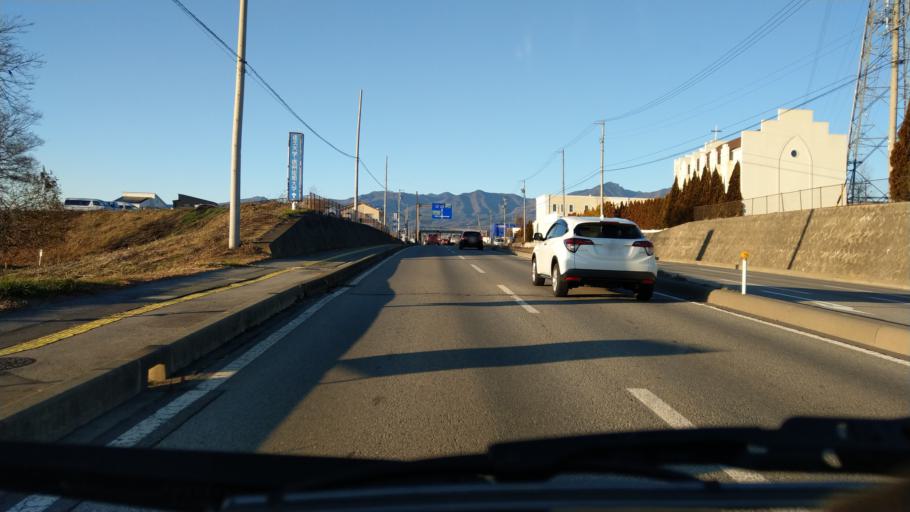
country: JP
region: Nagano
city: Saku
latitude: 36.2639
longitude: 138.4670
